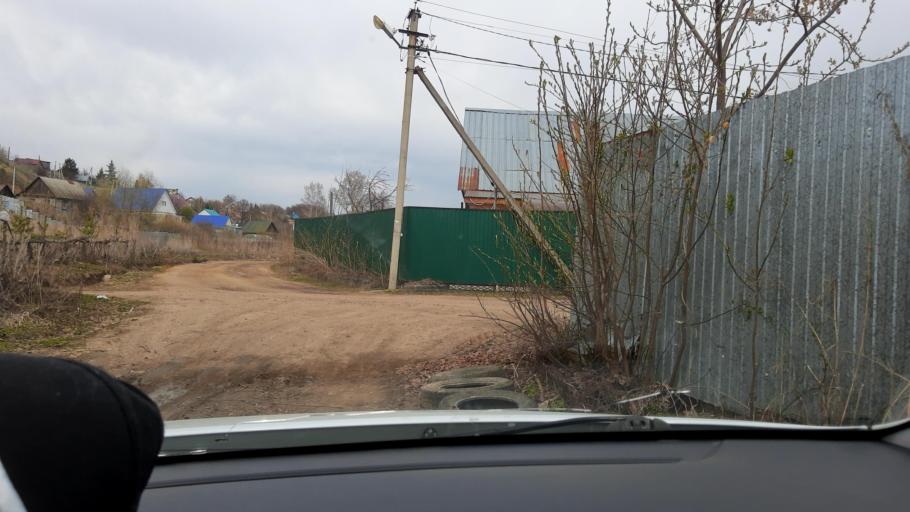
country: RU
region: Bashkortostan
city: Iglino
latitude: 54.8369
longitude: 56.4045
